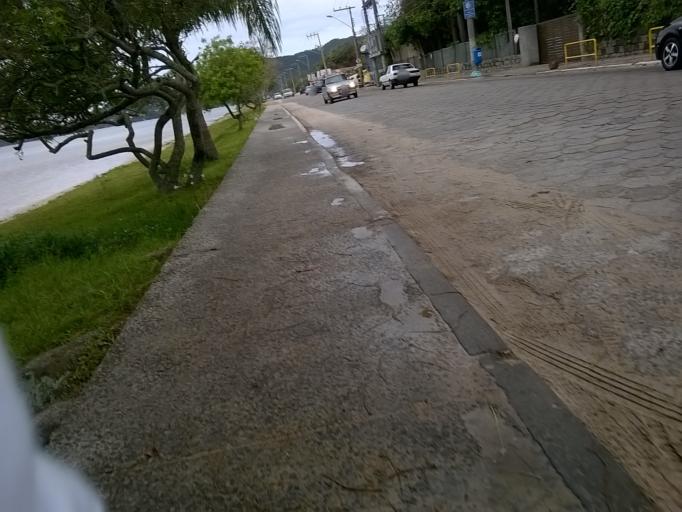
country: BR
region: Santa Catarina
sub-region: Florianopolis
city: Lagoa
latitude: -27.6077
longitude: -48.4584
